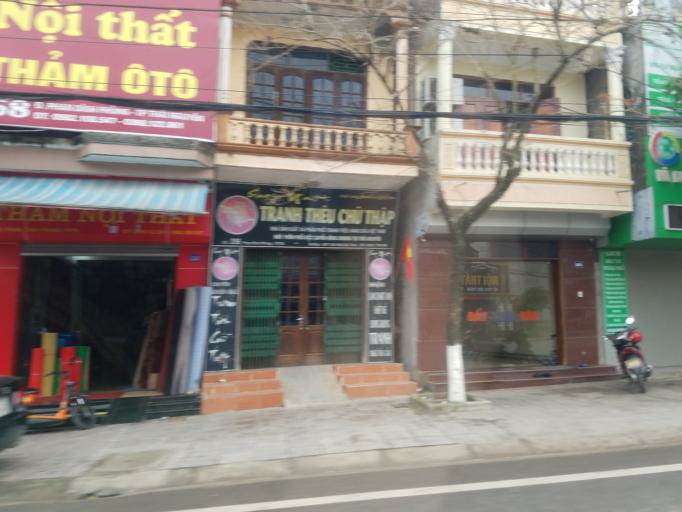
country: VN
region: Thai Nguyen
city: Thanh Pho Thai Nguyen
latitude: 21.5838
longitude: 105.8392
